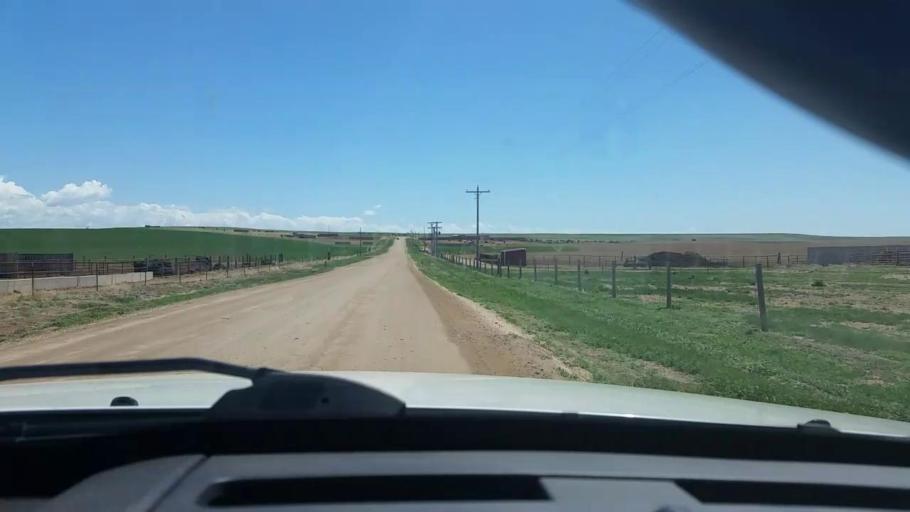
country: US
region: Colorado
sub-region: Larimer County
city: Wellington
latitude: 40.7981
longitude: -105.0468
